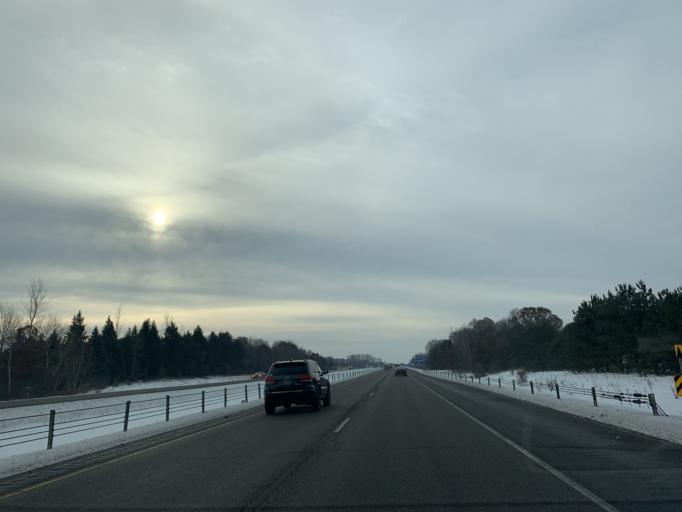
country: US
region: Minnesota
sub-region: Chisago County
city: Wyoming
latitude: 45.3095
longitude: -93.0035
